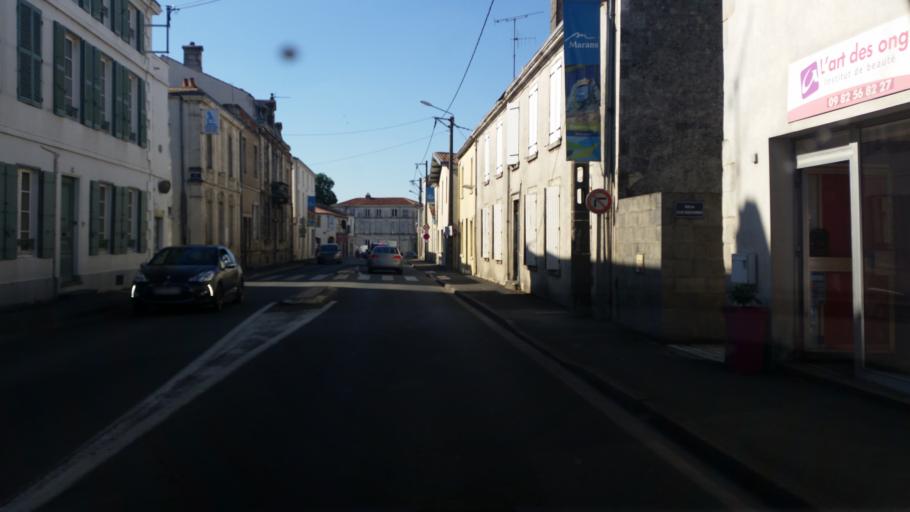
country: FR
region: Poitou-Charentes
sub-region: Departement de la Charente-Maritime
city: Marans
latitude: 46.3077
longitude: -0.9916
